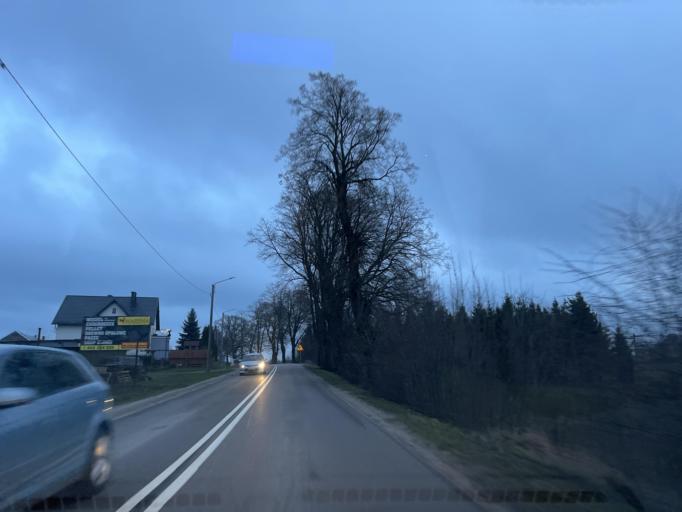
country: PL
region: Pomeranian Voivodeship
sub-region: Powiat kartuski
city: Kartuzy
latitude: 54.4028
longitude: 18.2192
